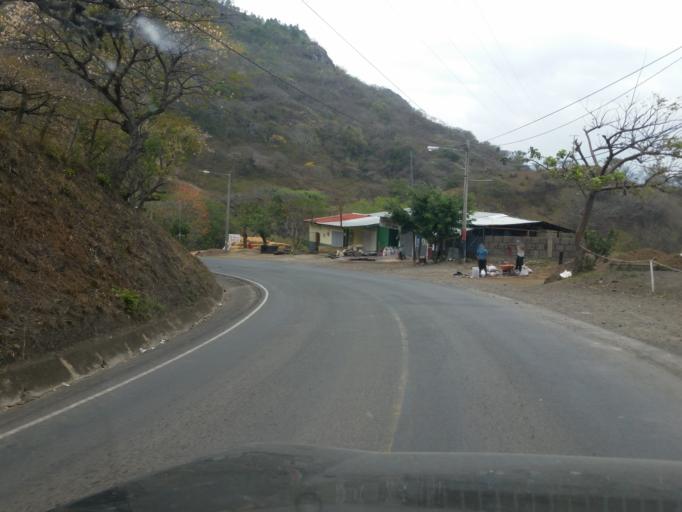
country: NI
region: Matagalpa
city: Matagalpa
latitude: 12.9412
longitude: -85.8952
